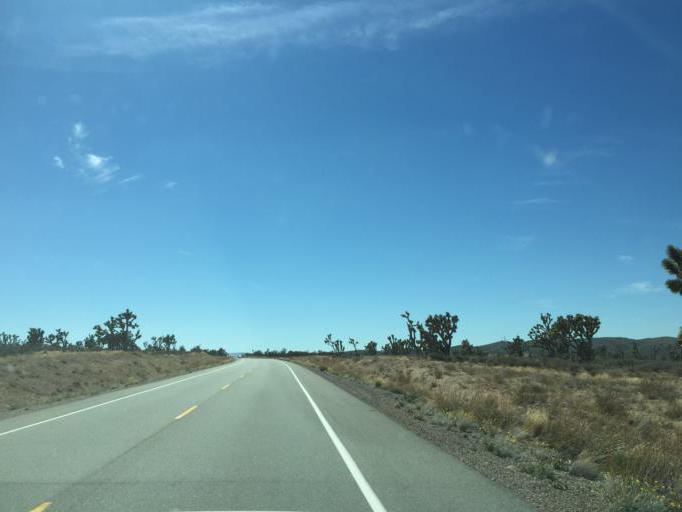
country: US
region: Arizona
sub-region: Mohave County
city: Meadview
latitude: 35.8750
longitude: -114.0592
